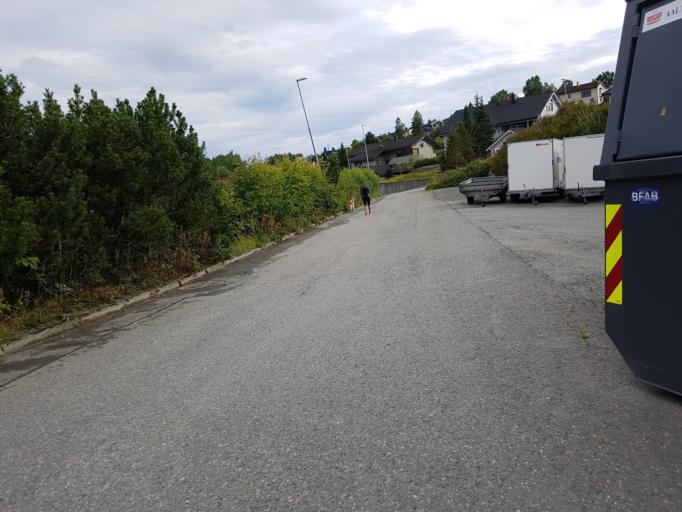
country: NO
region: Sor-Trondelag
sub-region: Trondheim
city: Trondheim
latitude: 63.3980
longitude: 10.4201
